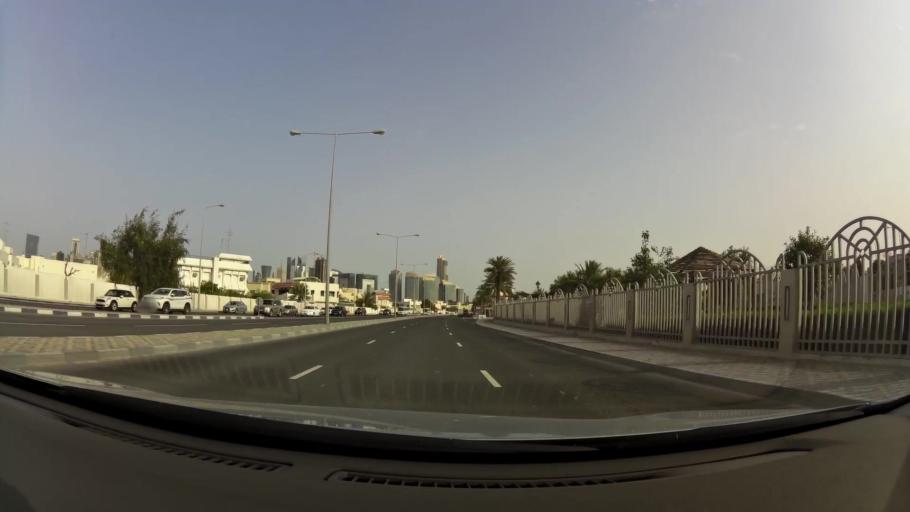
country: QA
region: Baladiyat ad Dawhah
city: Doha
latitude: 25.3267
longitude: 51.5073
